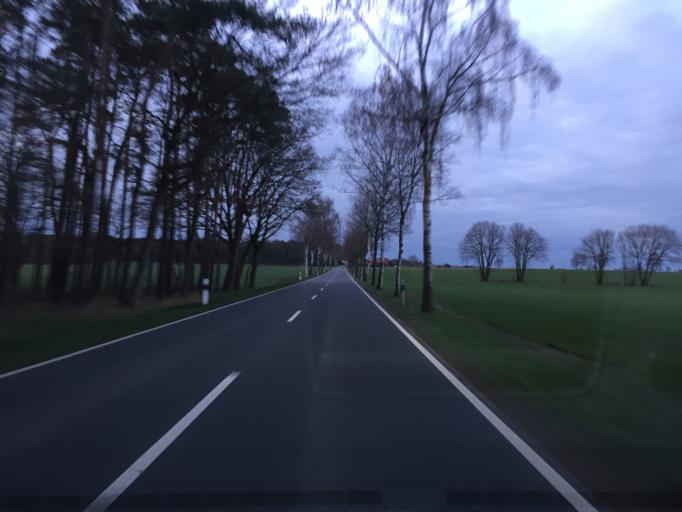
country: DE
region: Lower Saxony
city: Steimbke
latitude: 52.6096
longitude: 9.3925
